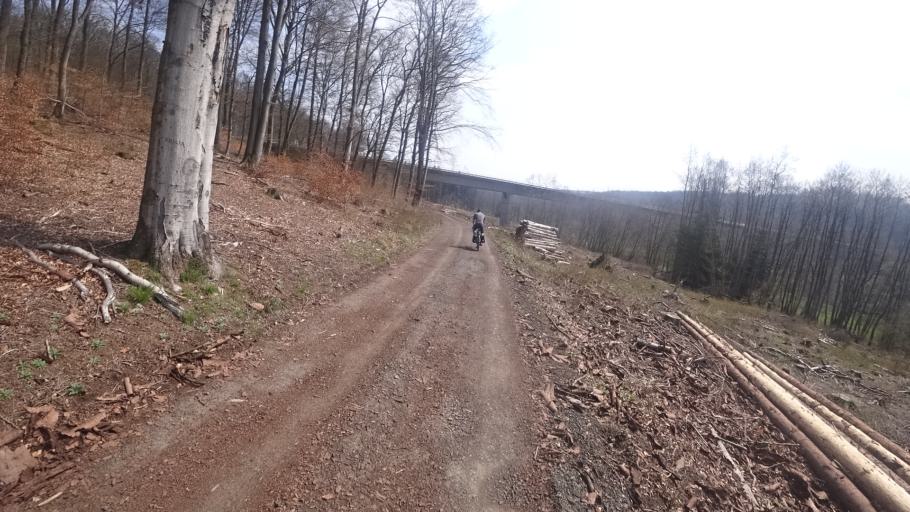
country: DE
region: Rheinland-Pfalz
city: Luckenbach
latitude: 50.6954
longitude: 7.8466
